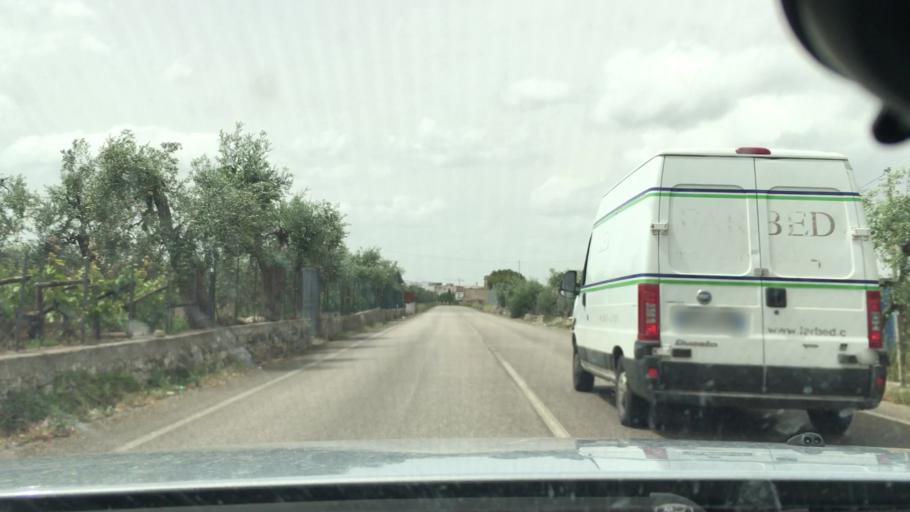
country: IT
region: Apulia
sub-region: Provincia di Bari
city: Capurso
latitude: 41.0427
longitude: 16.9390
